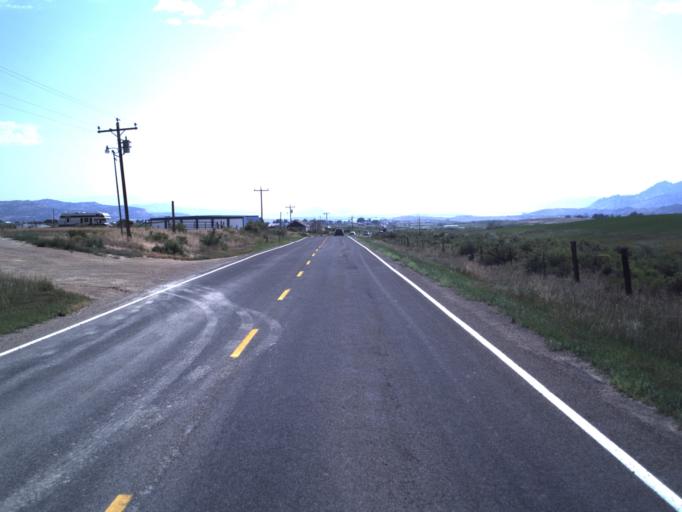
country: US
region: Utah
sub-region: Daggett County
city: Manila
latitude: 40.9885
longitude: -109.7081
